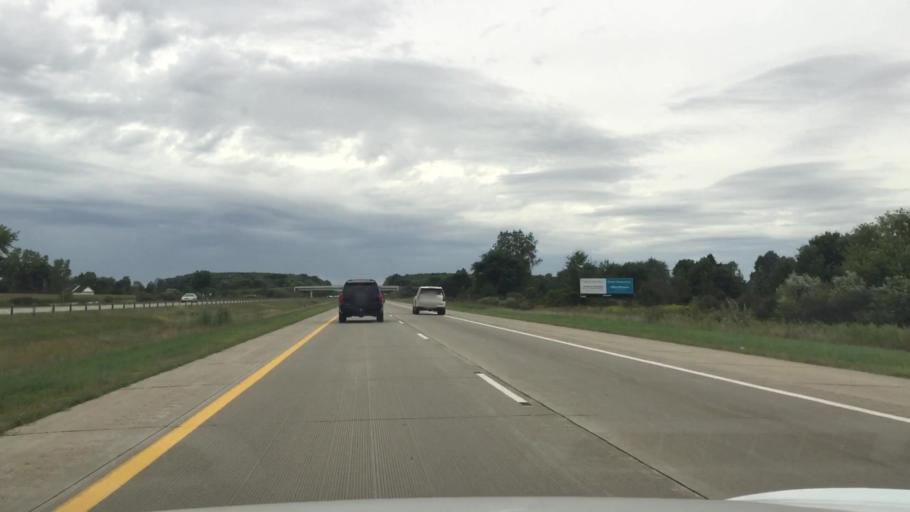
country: US
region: Michigan
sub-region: Macomb County
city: Richmond
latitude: 42.7683
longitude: -82.6874
